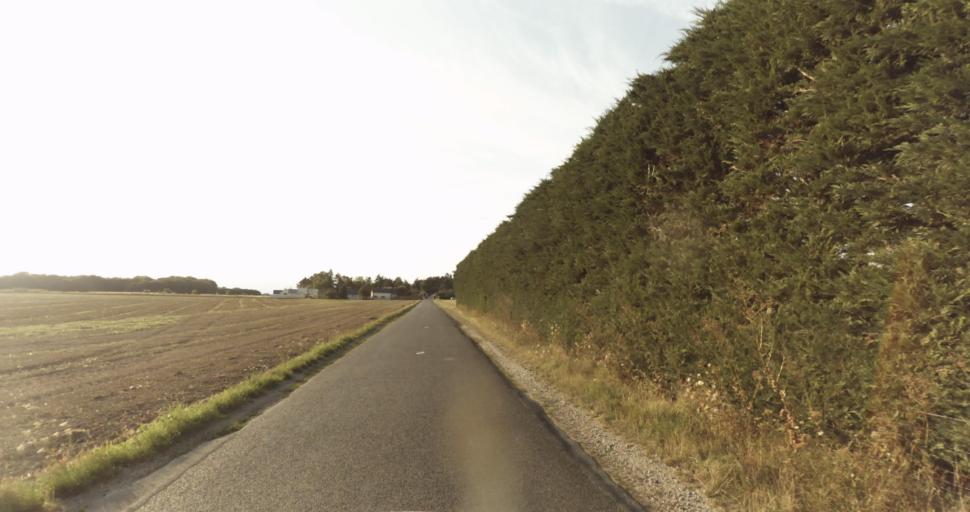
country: FR
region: Haute-Normandie
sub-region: Departement de l'Eure
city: Marcilly-sur-Eure
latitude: 48.8351
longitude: 1.2841
